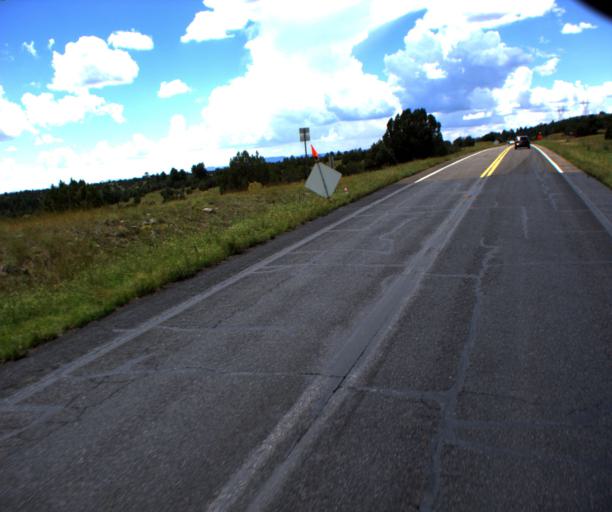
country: US
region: Arizona
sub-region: Gila County
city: Pine
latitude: 34.5168
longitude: -111.5299
